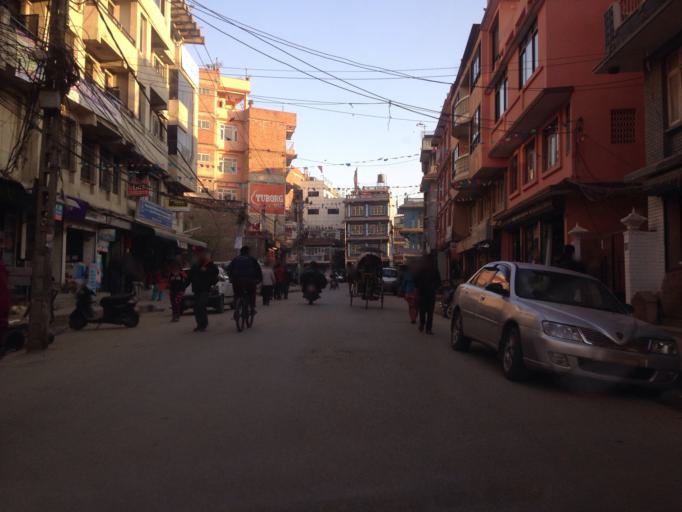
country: NP
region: Central Region
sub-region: Bagmati Zone
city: Kathmandu
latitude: 27.7135
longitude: 85.3035
